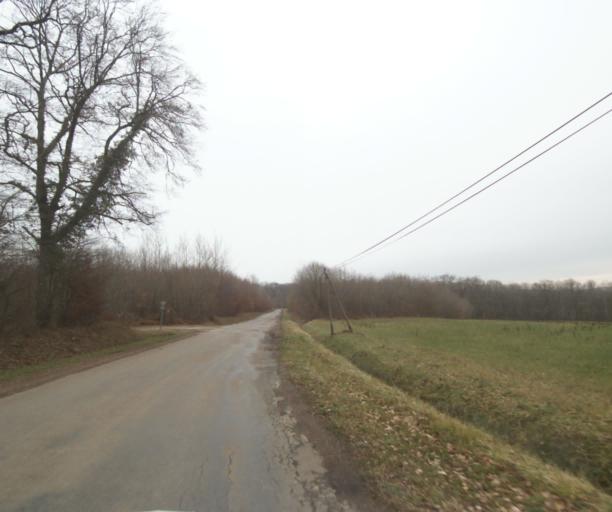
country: FR
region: Champagne-Ardenne
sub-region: Departement de la Haute-Marne
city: Wassy
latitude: 48.5184
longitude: 4.9707
